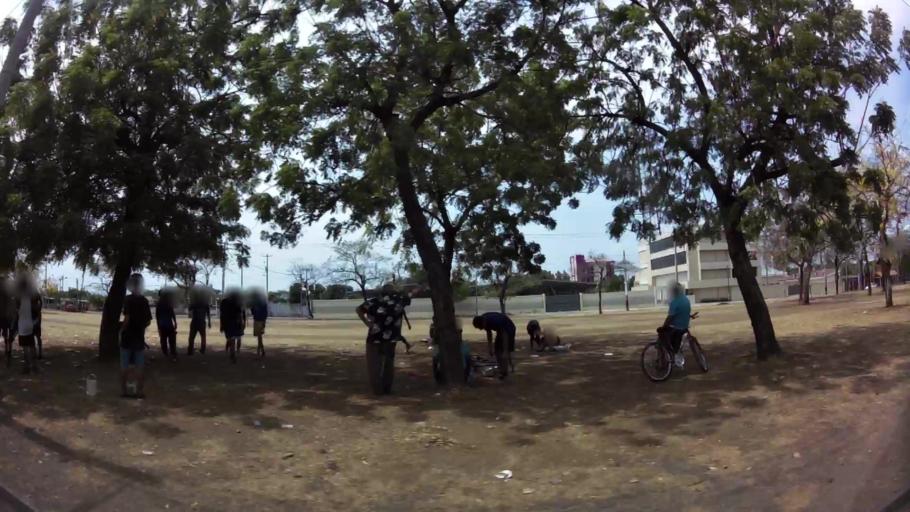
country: NI
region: Managua
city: Managua
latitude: 12.1543
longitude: -86.2758
